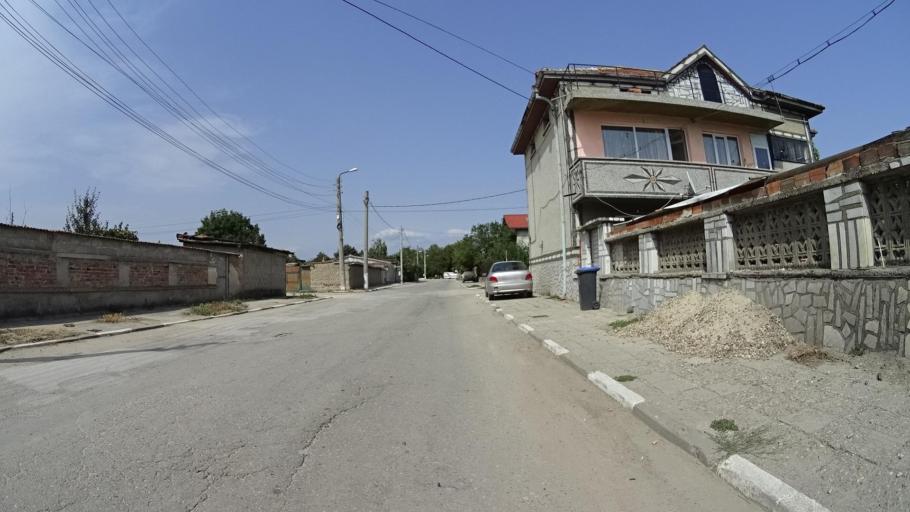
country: BG
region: Plovdiv
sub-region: Obshtina Kaloyanovo
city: Kaloyanovo
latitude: 42.2669
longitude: 24.8000
